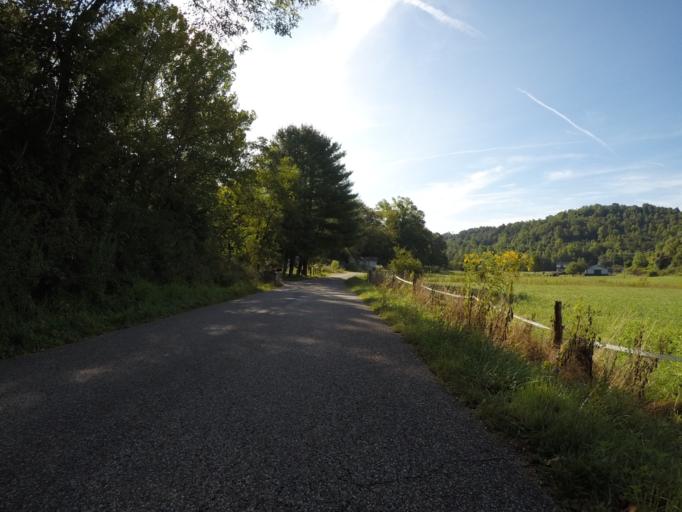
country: US
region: Ohio
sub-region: Lawrence County
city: Burlington
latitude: 38.5017
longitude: -82.5135
